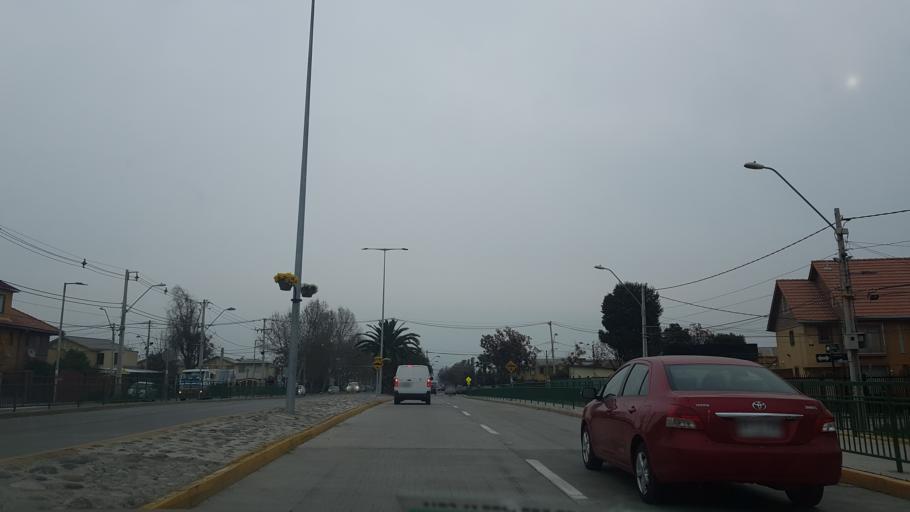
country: CL
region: Santiago Metropolitan
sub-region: Provincia de Santiago
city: Lo Prado
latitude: -33.3566
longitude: -70.7141
